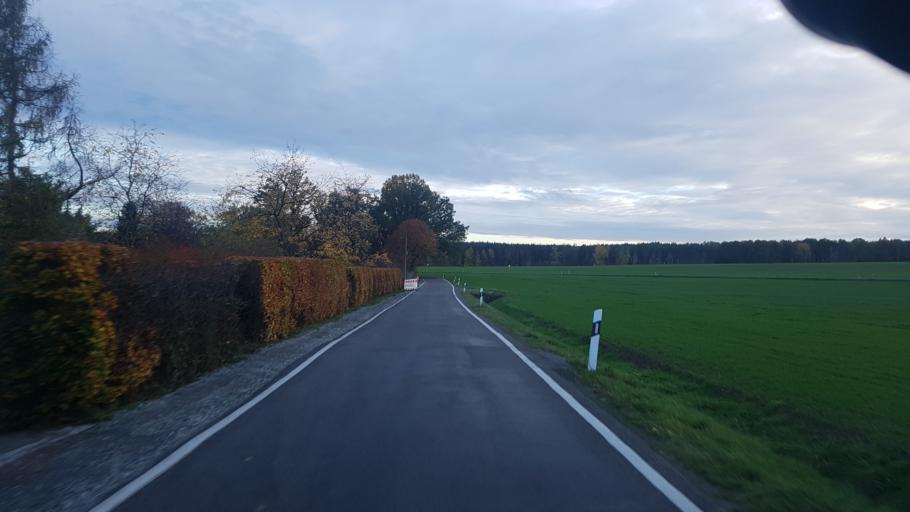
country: DE
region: Saxony
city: Dahlen
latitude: 51.3810
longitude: 13.0351
